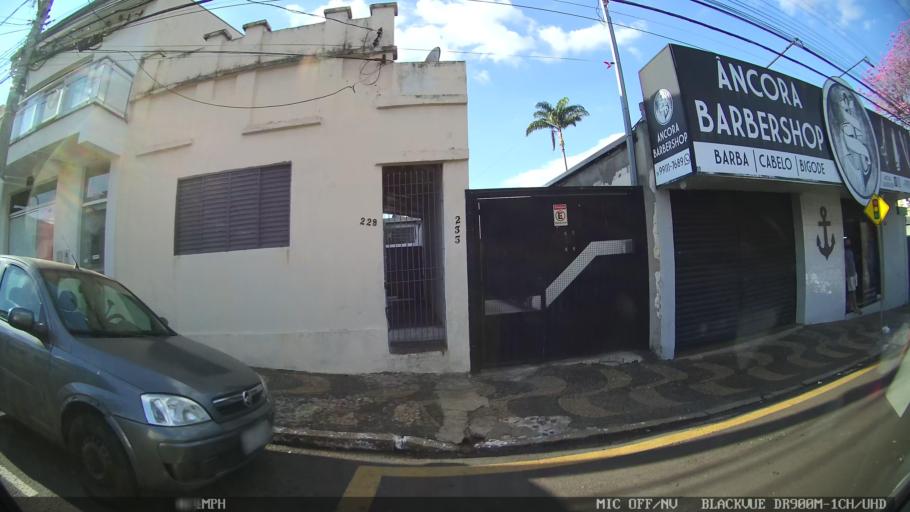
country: BR
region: Sao Paulo
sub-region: Santa Barbara D'Oeste
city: Santa Barbara d'Oeste
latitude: -22.7547
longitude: -47.4110
